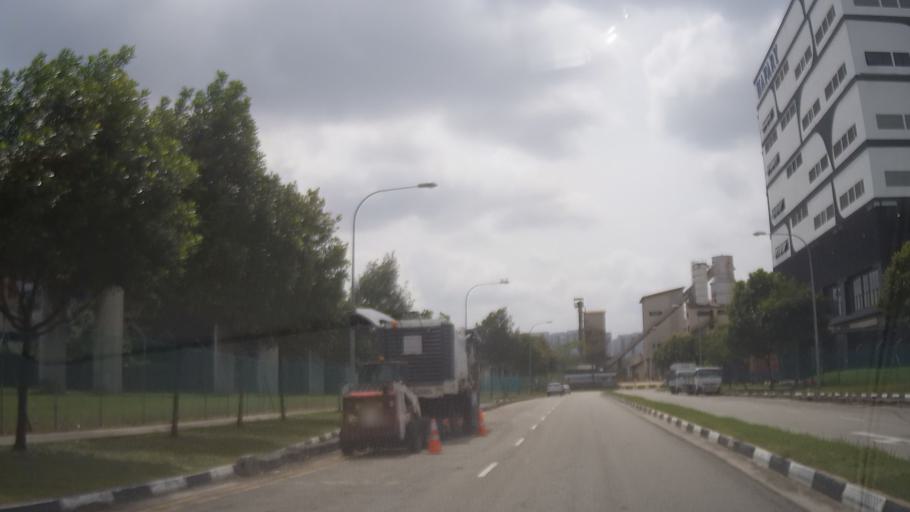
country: MY
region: Johor
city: Johor Bahru
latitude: 1.4137
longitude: 103.7485
